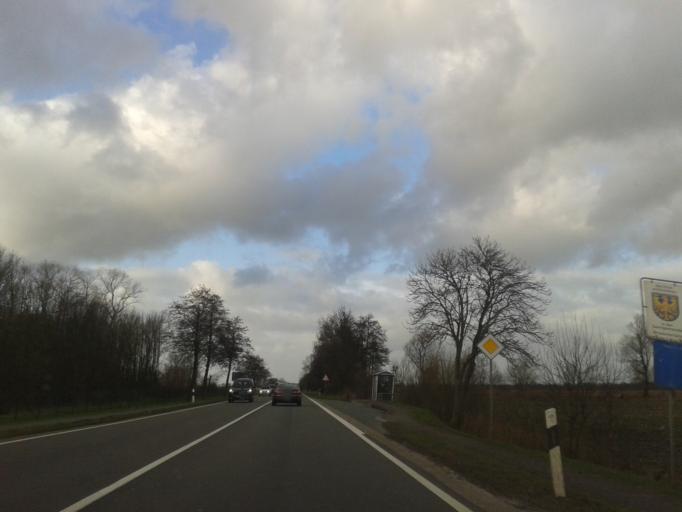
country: DE
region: Lower Saxony
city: Upgant-Schott
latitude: 53.4965
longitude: 7.3031
